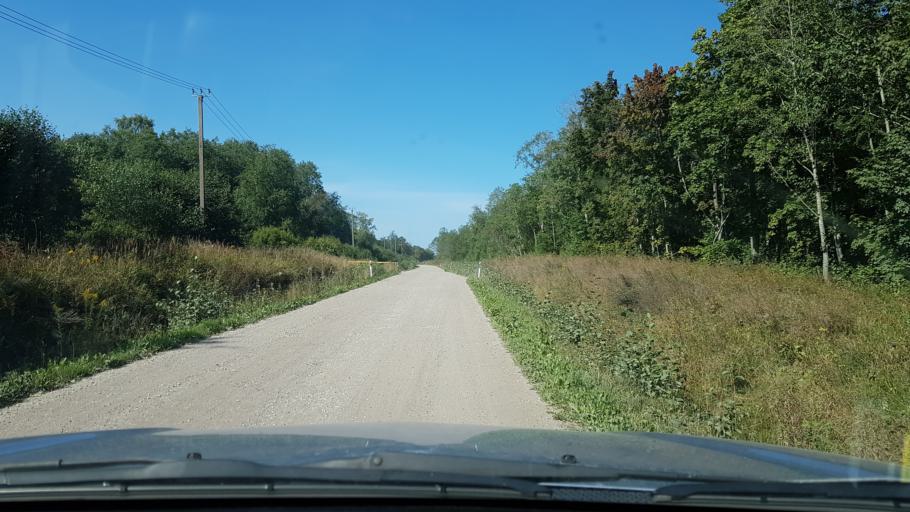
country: EE
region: Ida-Virumaa
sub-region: Sillamaee linn
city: Sillamae
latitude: 59.3757
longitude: 27.7796
